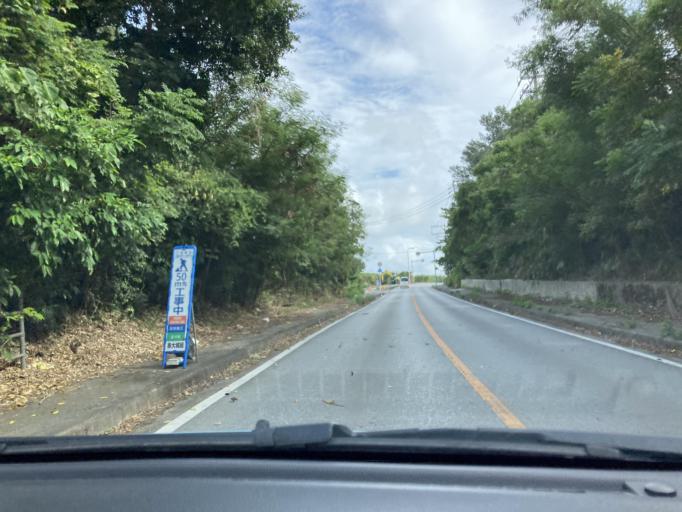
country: JP
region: Okinawa
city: Itoman
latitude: 26.1108
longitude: 127.6934
